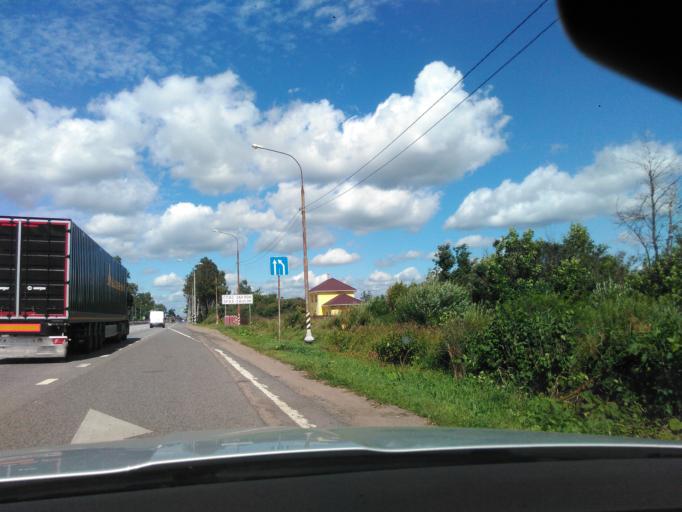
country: RU
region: Moskovskaya
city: Reshetnikovo
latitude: 56.4650
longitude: 36.5876
